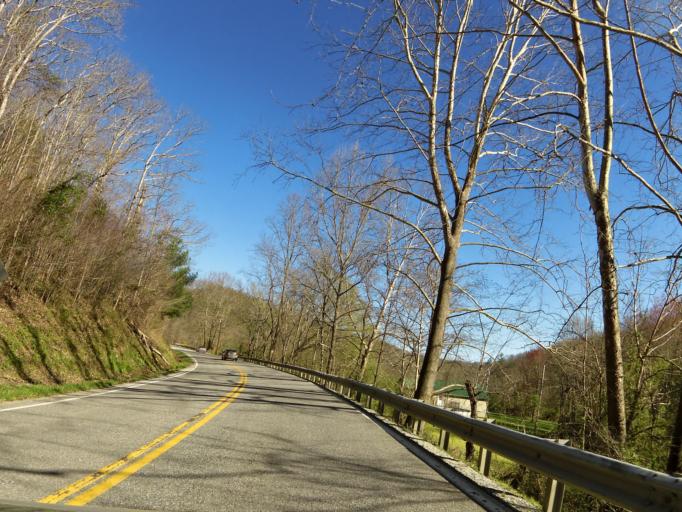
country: US
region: Tennessee
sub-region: Scott County
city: Huntsville
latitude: 36.4446
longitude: -84.4667
